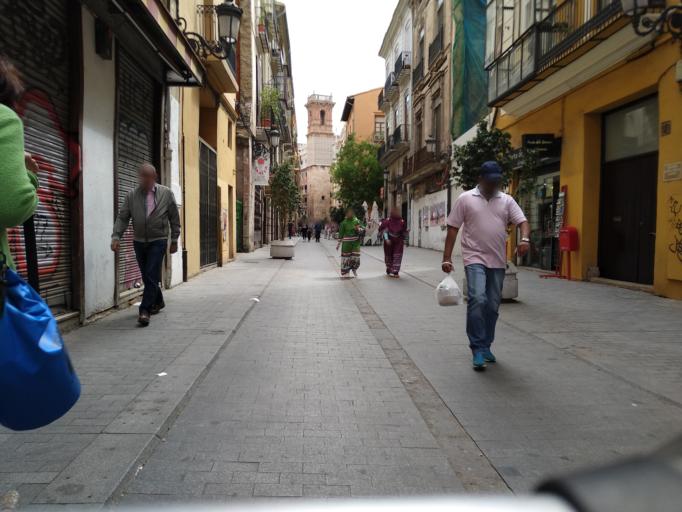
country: ES
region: Valencia
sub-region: Provincia de Valencia
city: Valencia
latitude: 39.4785
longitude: -0.3764
